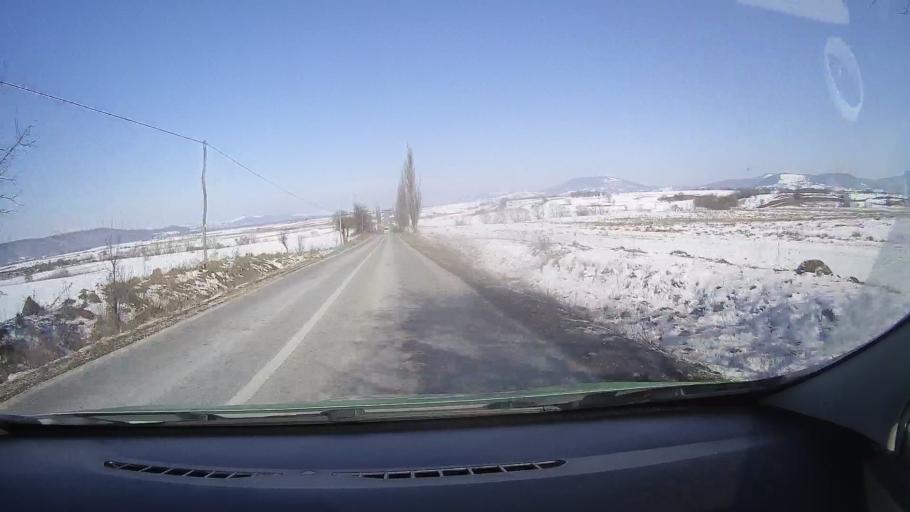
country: RO
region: Brasov
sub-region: Comuna Parau
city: Parau
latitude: 45.8586
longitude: 25.1973
